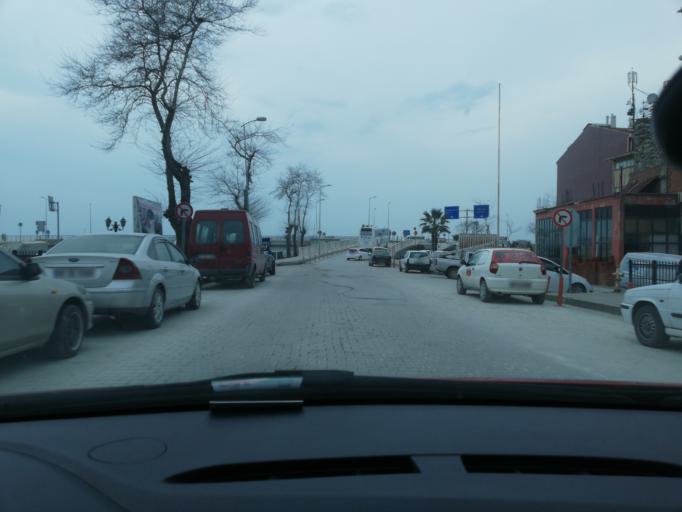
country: TR
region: Kastamonu
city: Inebolu
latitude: 41.9780
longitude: 33.7592
